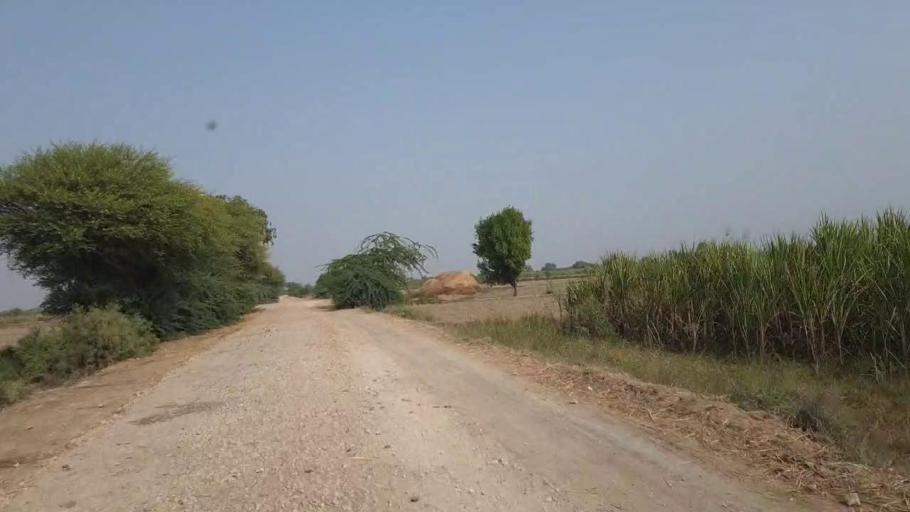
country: PK
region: Sindh
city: Kario
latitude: 24.9086
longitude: 68.5989
